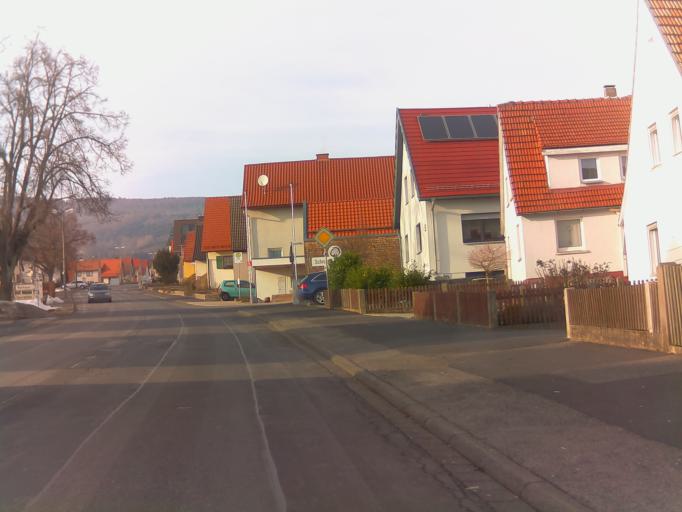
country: DE
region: Bavaria
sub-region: Regierungsbezirk Unterfranken
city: Sandberg
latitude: 50.3489
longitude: 10.0071
